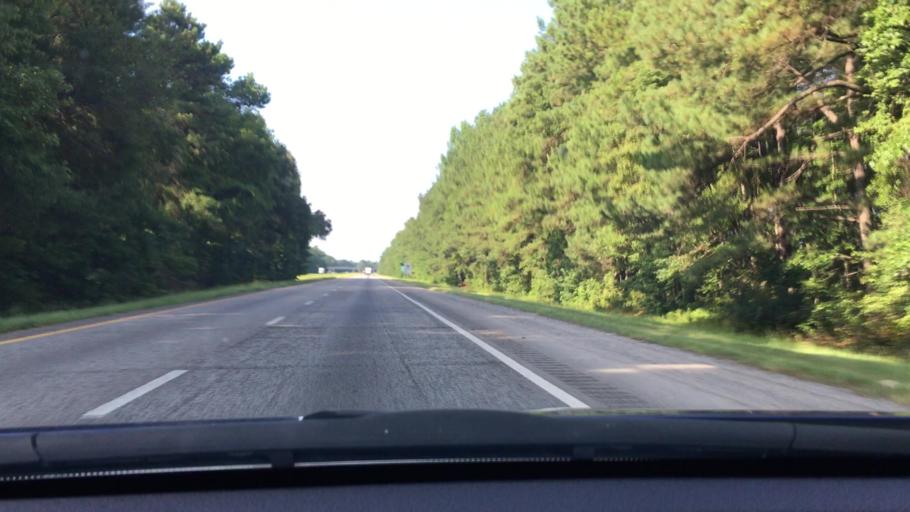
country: US
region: South Carolina
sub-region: Clarendon County
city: Manning
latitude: 33.6958
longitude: -80.2530
